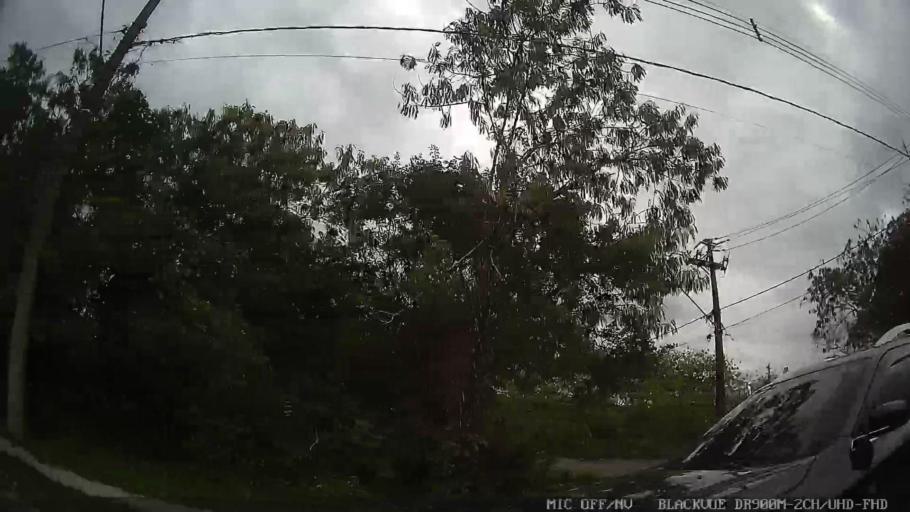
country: BR
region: Sao Paulo
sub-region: Guaruja
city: Guaruja
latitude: -23.9953
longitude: -46.2915
